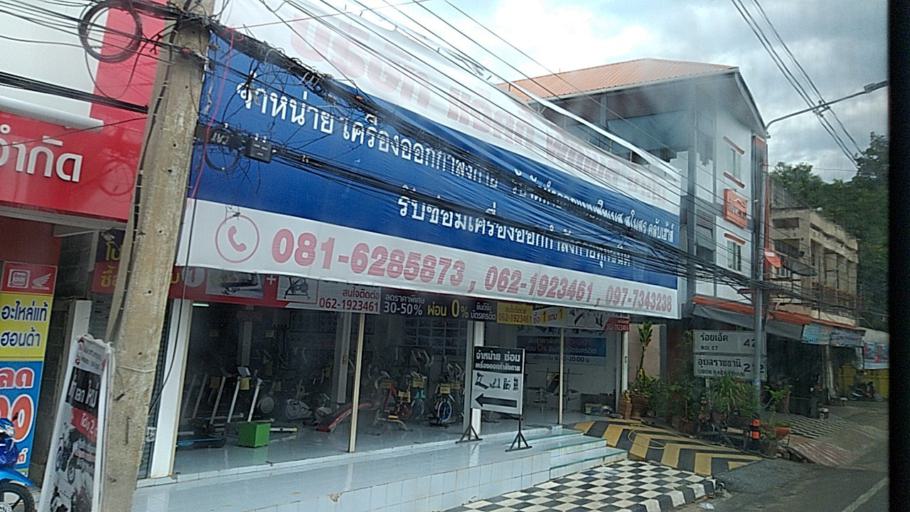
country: TH
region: Maha Sarakham
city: Maha Sarakham
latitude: 16.1906
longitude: 103.2956
